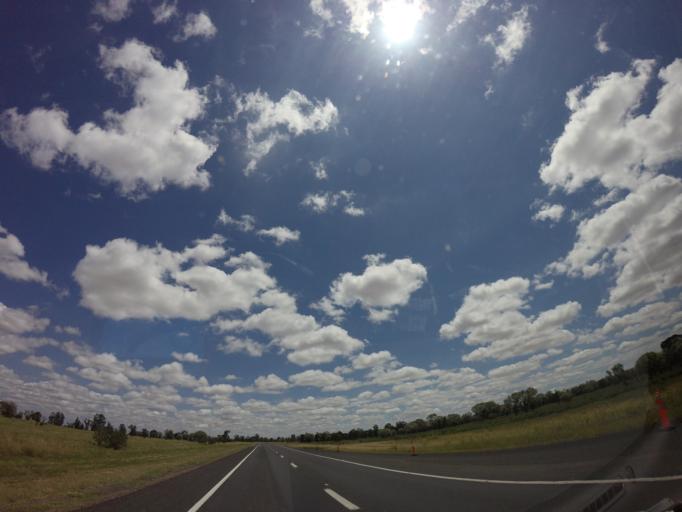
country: AU
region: New South Wales
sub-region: Moree Plains
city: Moree
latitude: -29.1126
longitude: 150.0288
